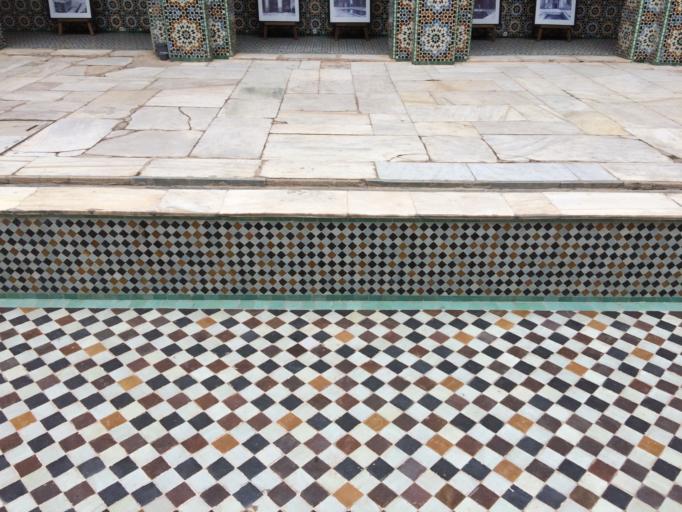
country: MA
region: Marrakech-Tensift-Al Haouz
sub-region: Marrakech
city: Marrakesh
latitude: 31.6320
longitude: -7.9863
